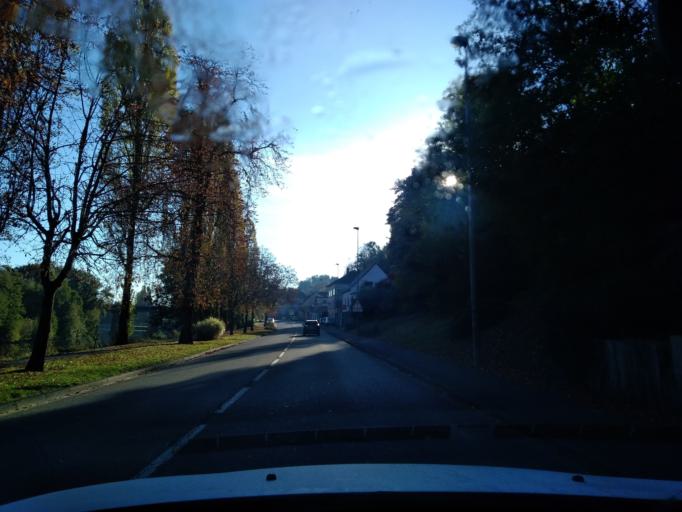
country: FR
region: Lorraine
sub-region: Departement de la Moselle
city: Sarreguemines
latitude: 49.1120
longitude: 7.0538
